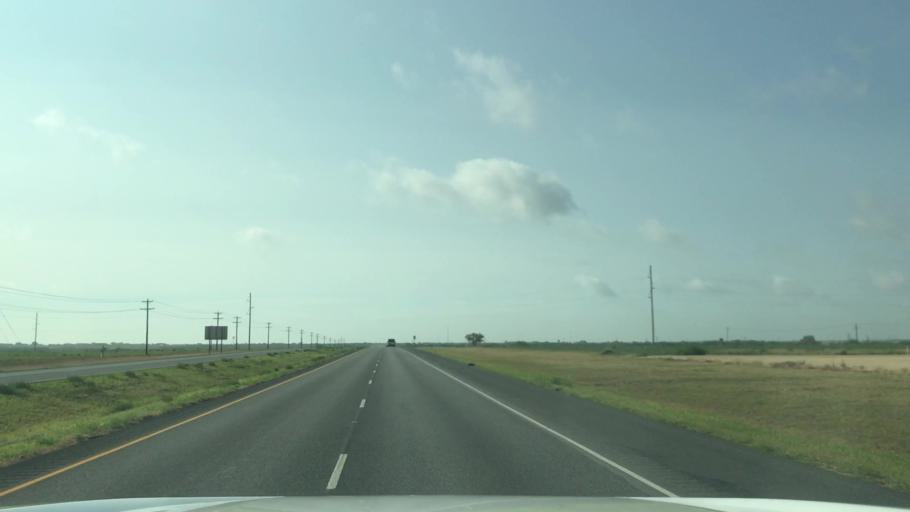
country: US
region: Texas
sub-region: Scurry County
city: Snyder
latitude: 32.7787
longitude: -100.9436
